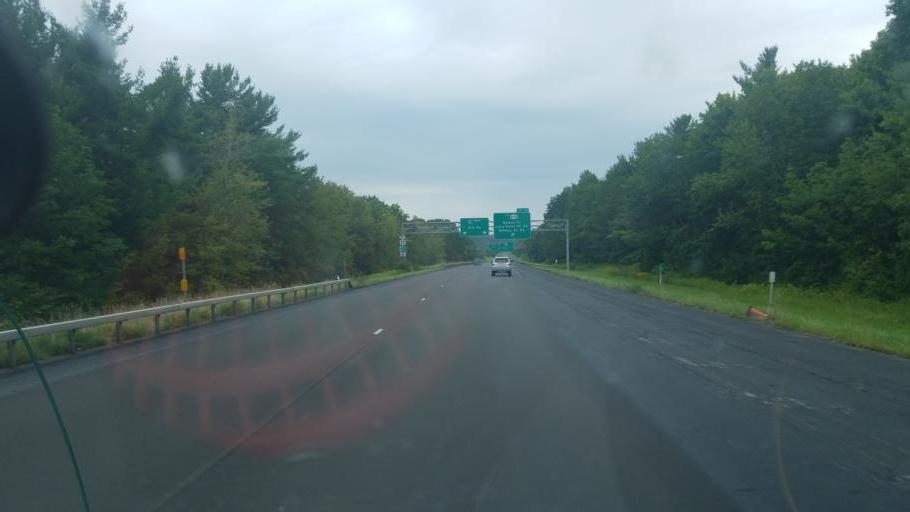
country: US
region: New York
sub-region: Chautauqua County
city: Lakewood
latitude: 42.1488
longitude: -79.3642
